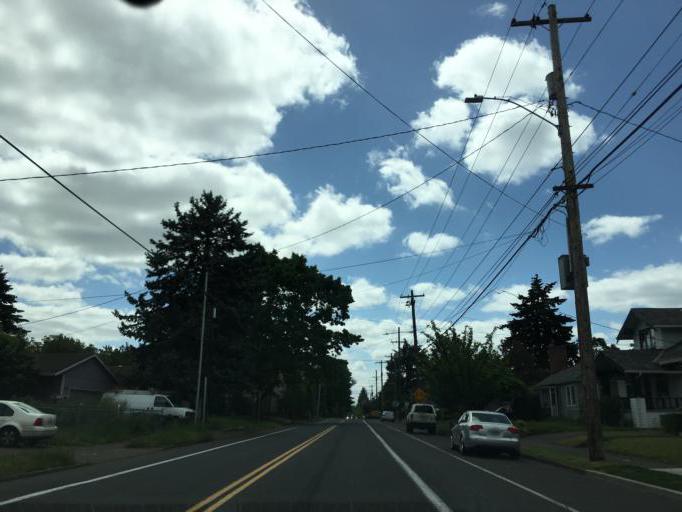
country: US
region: Oregon
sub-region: Multnomah County
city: Lents
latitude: 45.4946
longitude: -122.6091
